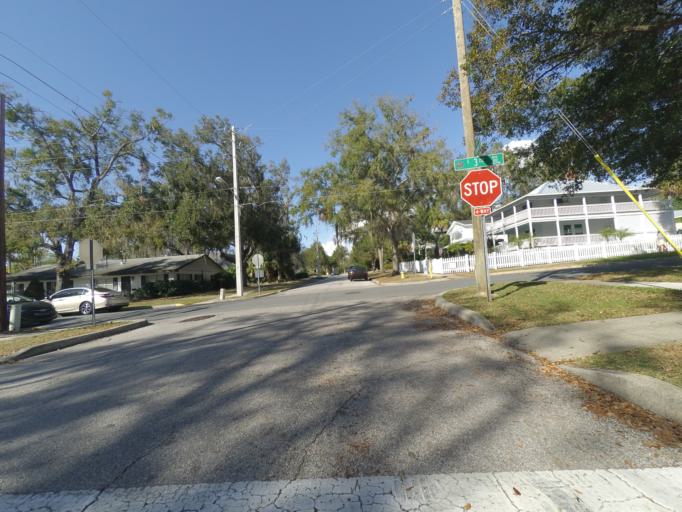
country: US
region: Florida
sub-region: Lake County
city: Mount Dora
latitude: 28.7986
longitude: -81.6427
